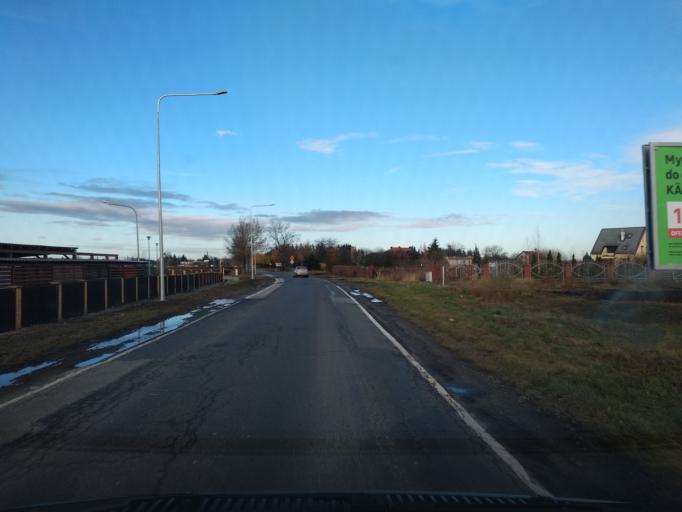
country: PL
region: Lower Silesian Voivodeship
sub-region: Powiat wroclawski
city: Zerniki Wroclawskie
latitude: 51.0455
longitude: 17.0384
